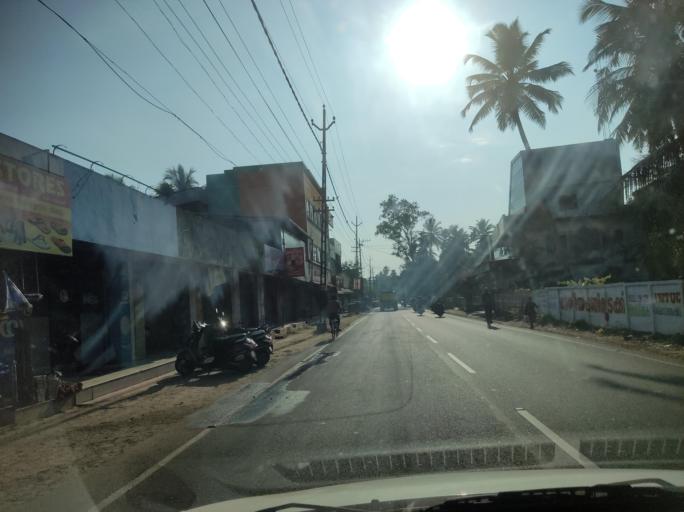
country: IN
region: Kerala
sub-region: Alappuzha
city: Kattanam
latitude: 9.1773
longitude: 76.5539
